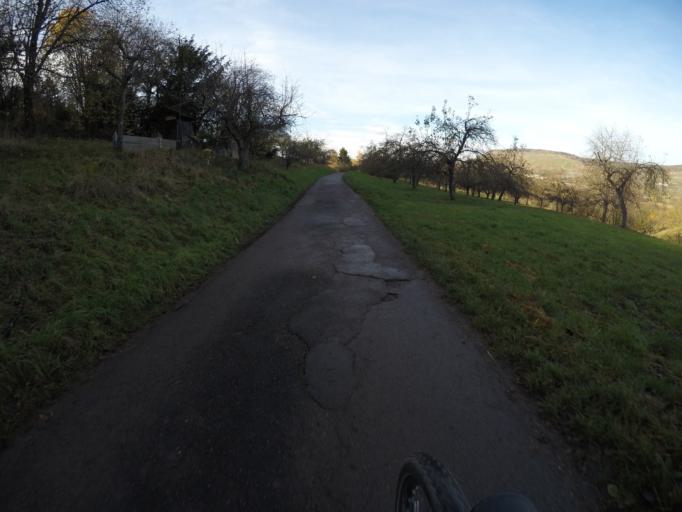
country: DE
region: Baden-Wuerttemberg
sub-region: Regierungsbezirk Stuttgart
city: Weinstadt-Endersbach
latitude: 48.8068
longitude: 9.4050
